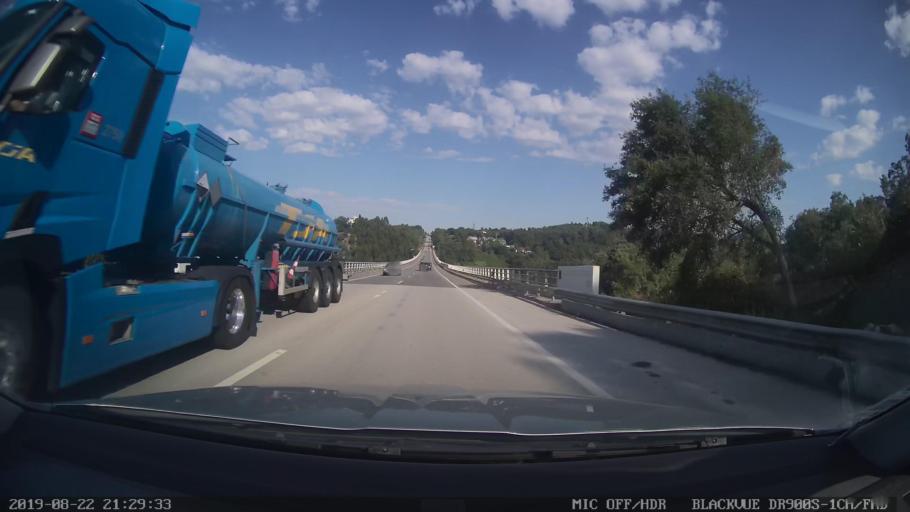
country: PT
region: Leiria
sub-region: Pedrogao Grande
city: Pedrogao Grande
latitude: 39.9032
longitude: -8.1370
